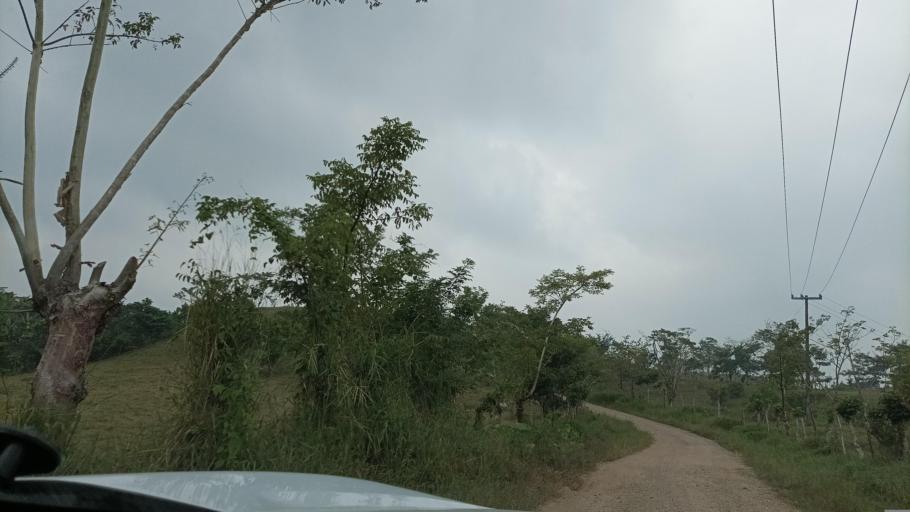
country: MX
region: Veracruz
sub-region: Uxpanapa
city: Poblado 10
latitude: 17.5706
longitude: -94.2276
